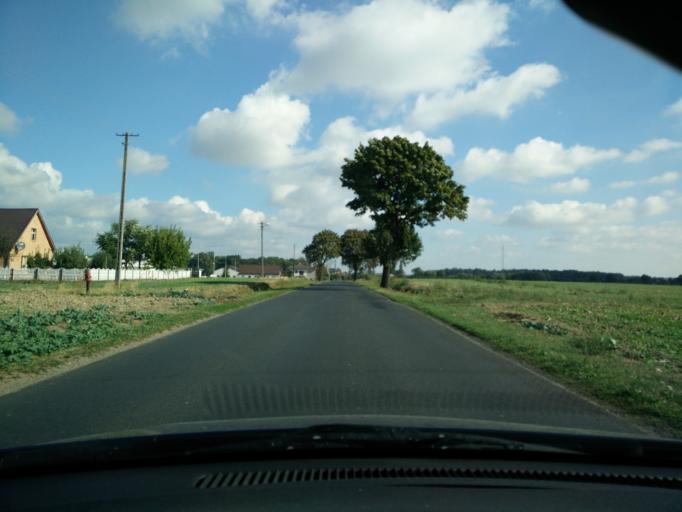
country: PL
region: Greater Poland Voivodeship
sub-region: Powiat sredzki
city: Dominowo
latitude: 52.2994
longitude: 17.3437
